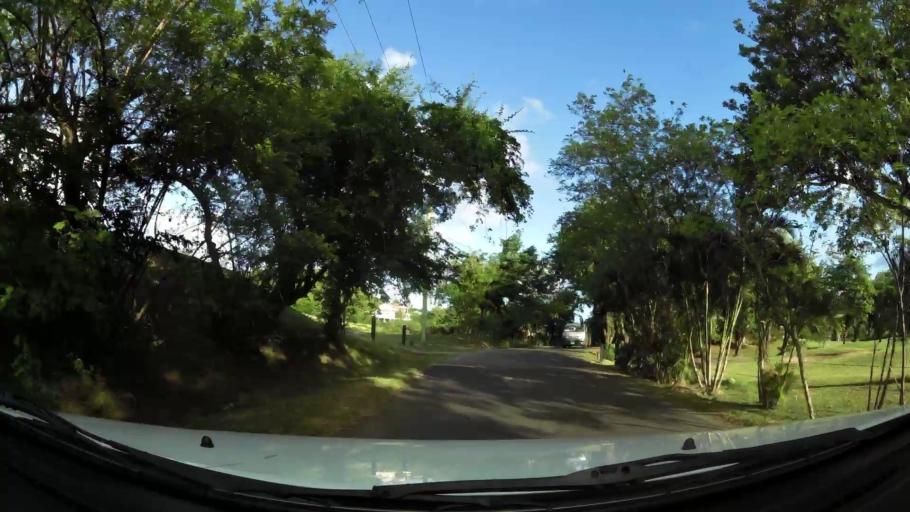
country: LC
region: Gros-Islet
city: Gros Islet
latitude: 14.0969
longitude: -60.9391
